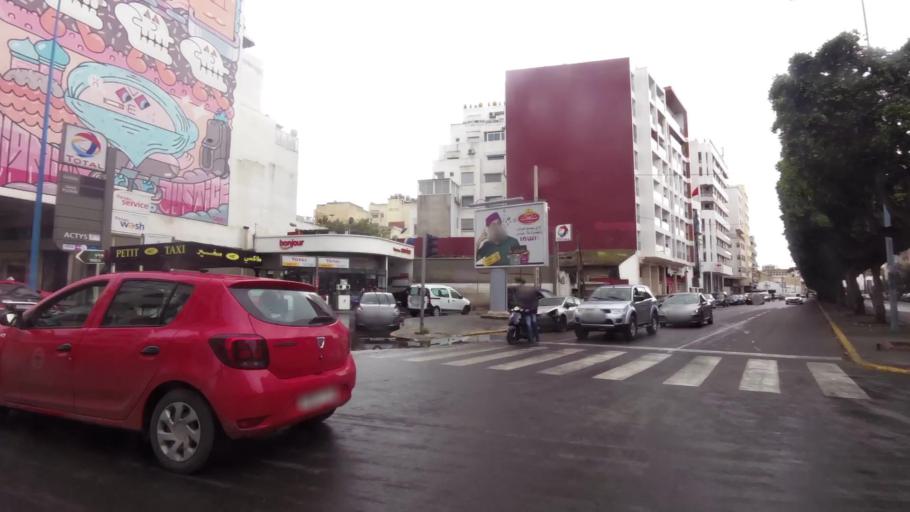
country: MA
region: Grand Casablanca
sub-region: Casablanca
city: Casablanca
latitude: 33.5977
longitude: -7.6291
